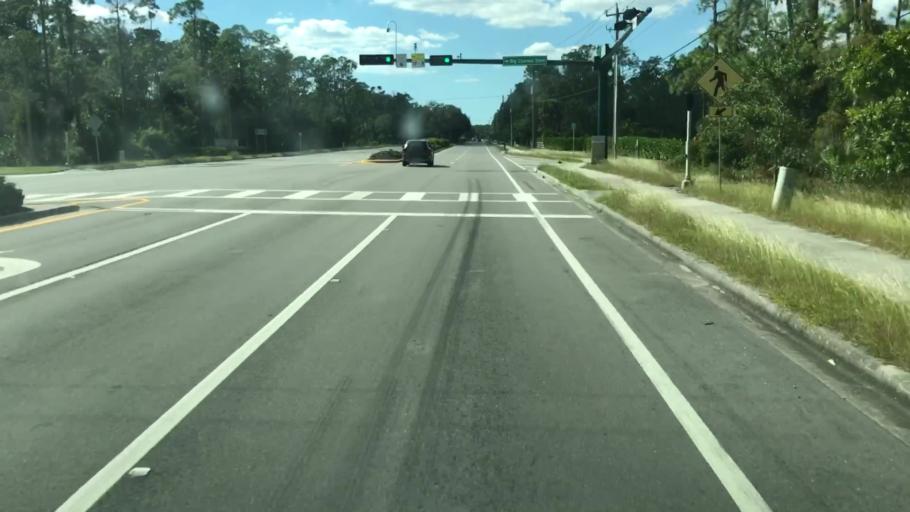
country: US
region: Florida
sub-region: Collier County
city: Vineyards
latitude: 26.2291
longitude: -81.6757
